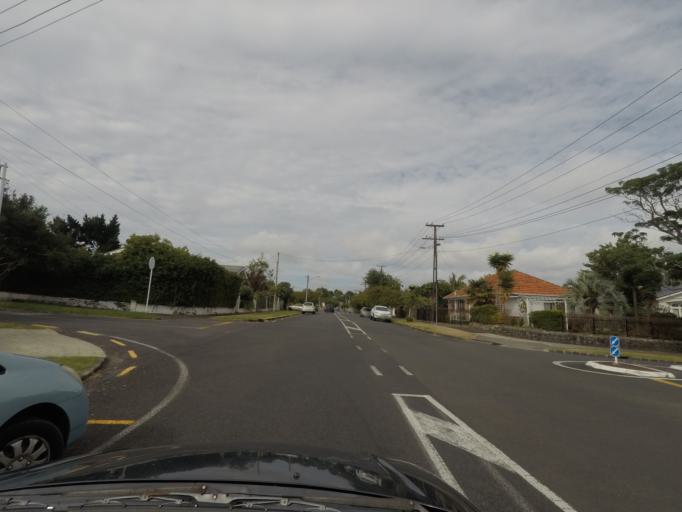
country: NZ
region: Auckland
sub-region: Auckland
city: Rosebank
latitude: -36.8769
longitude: 174.7187
